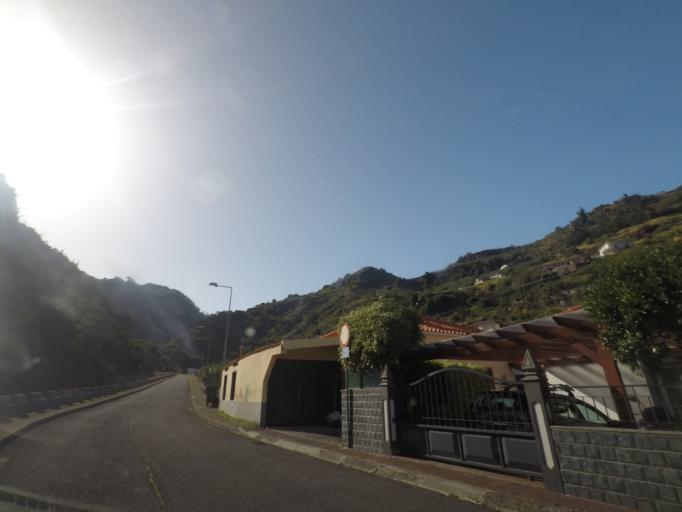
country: PT
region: Madeira
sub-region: Santa Cruz
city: Santa Cruz
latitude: 32.6906
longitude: -16.7982
